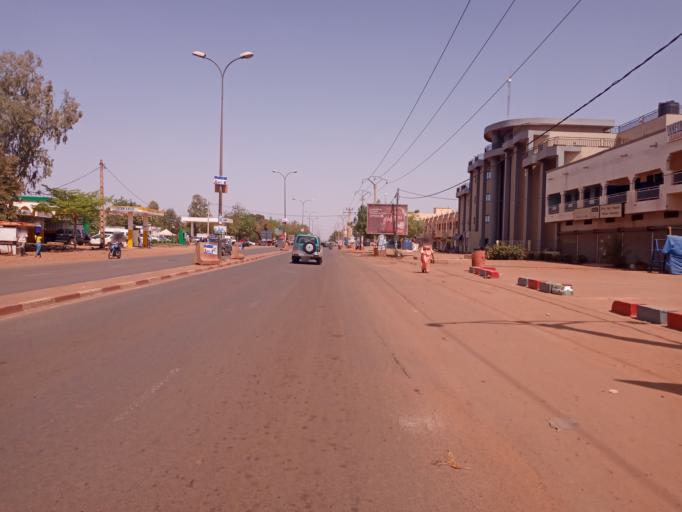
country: ML
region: Bamako
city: Bamako
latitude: 12.6637
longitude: -7.9440
